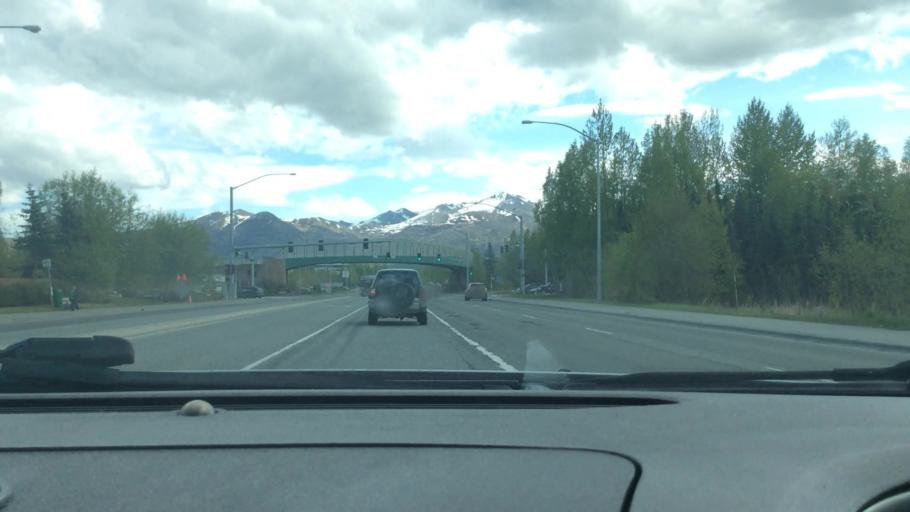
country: US
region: Alaska
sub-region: Anchorage Municipality
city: Anchorage
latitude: 61.1808
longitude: -149.8107
